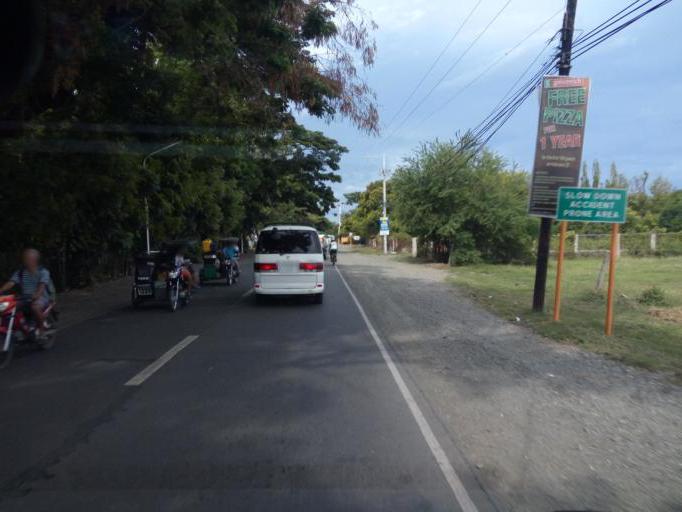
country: PH
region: Central Luzon
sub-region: Province of Nueva Ecija
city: Sibul
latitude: 15.7965
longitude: 120.9812
